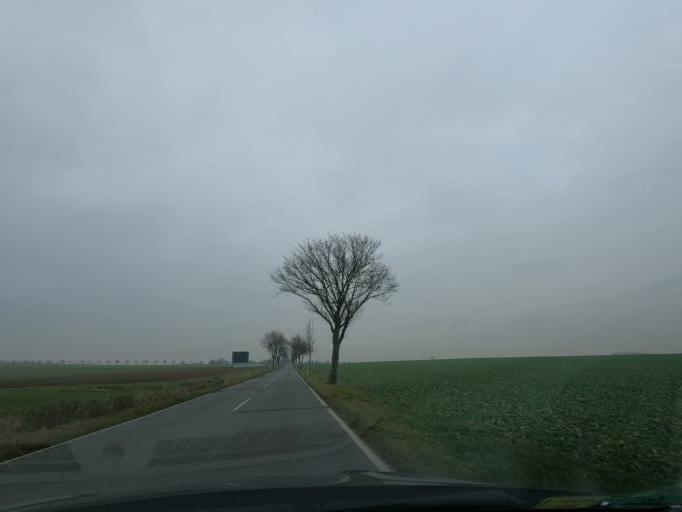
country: DE
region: Lower Saxony
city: Wolfenbuettel
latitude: 52.1709
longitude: 10.5845
